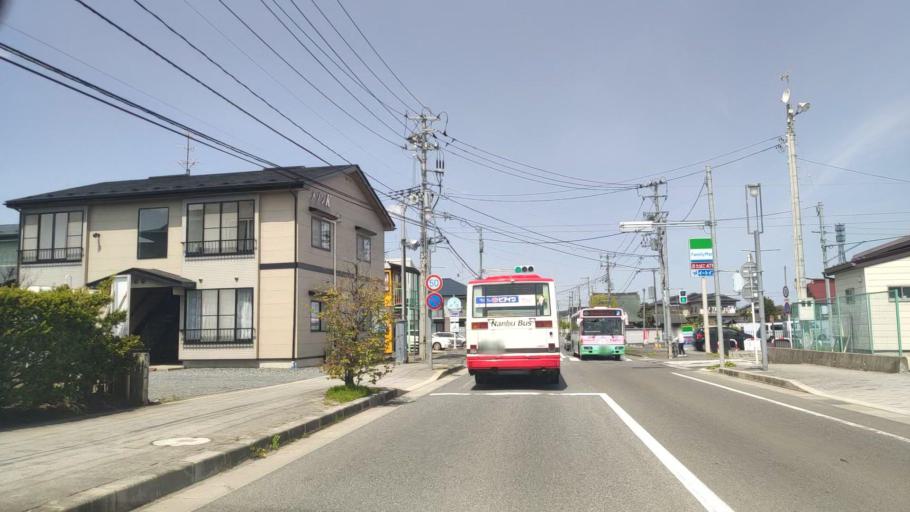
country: JP
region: Aomori
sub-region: Hachinohe Shi
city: Uchimaru
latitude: 40.5037
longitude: 141.4399
